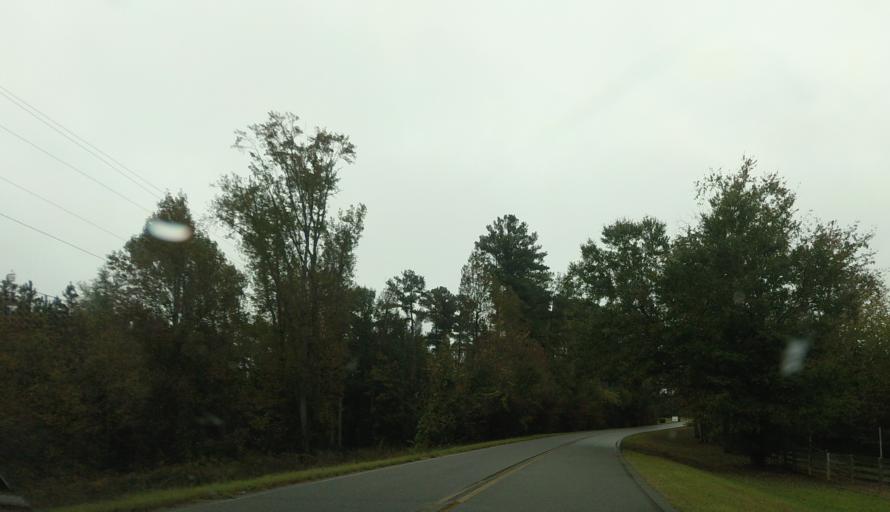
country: US
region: Georgia
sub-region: Macon County
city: Marshallville
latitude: 32.5296
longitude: -83.9647
